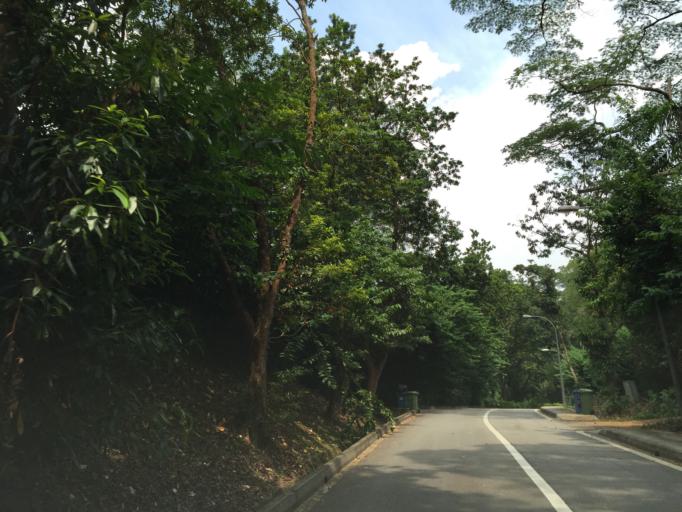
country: SG
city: Singapore
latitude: 1.3246
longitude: 103.8326
